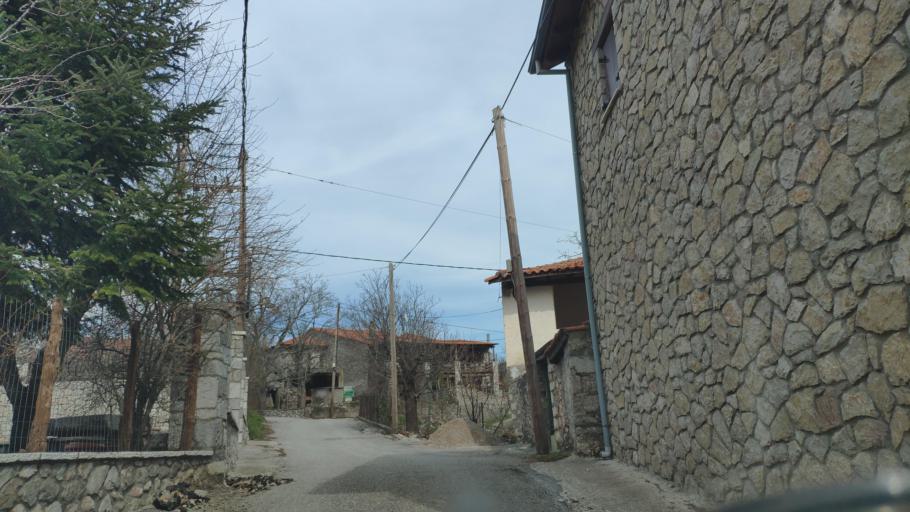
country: GR
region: Central Greece
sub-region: Nomos Fokidos
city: Amfissa
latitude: 38.6418
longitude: 22.4241
